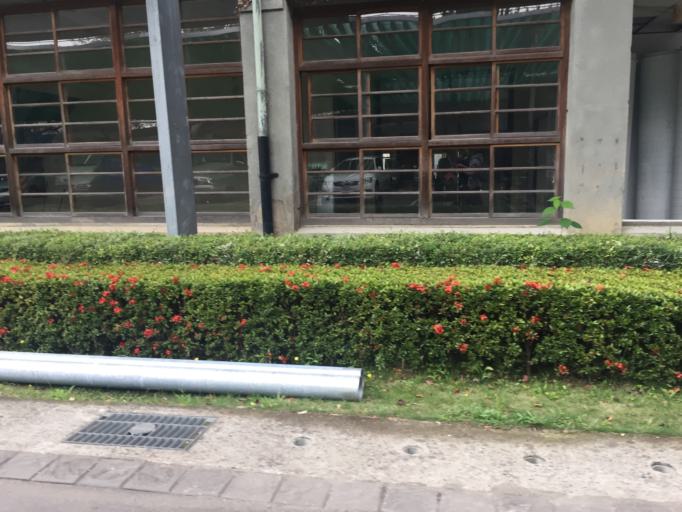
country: TW
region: Taiwan
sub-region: Taichung City
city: Taichung
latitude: 24.1323
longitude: 120.6823
